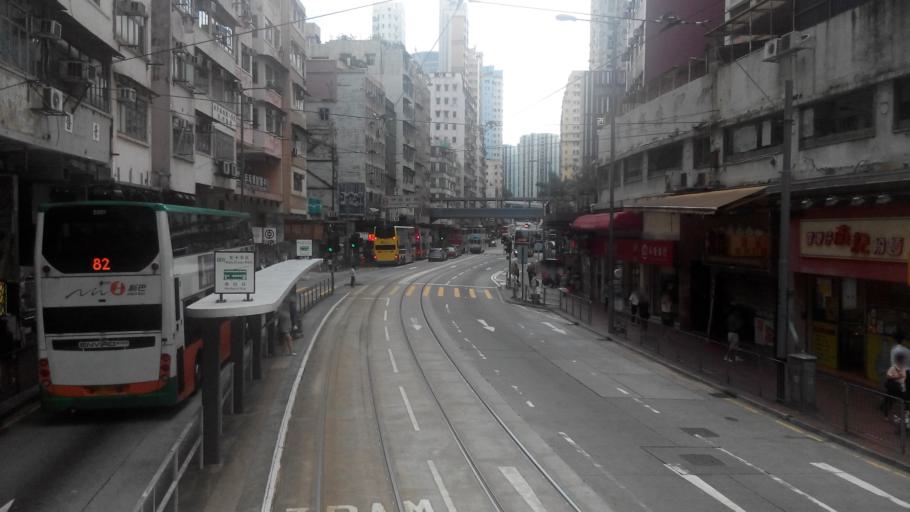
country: HK
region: Wanchai
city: Wan Chai
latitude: 22.2812
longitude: 114.2227
